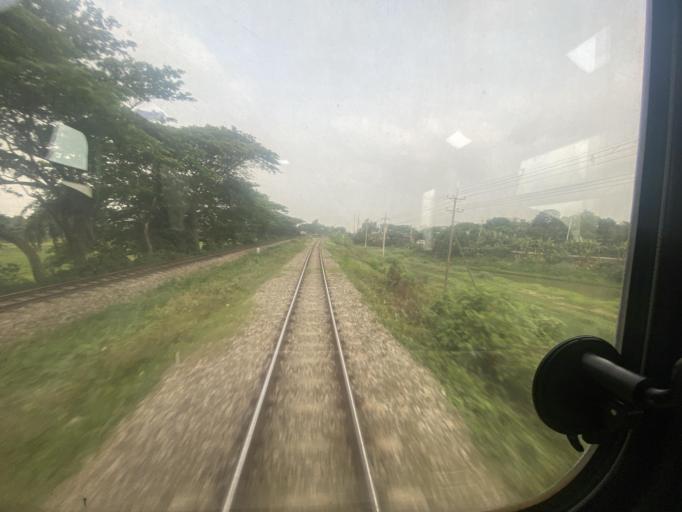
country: BD
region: Dhaka
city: Tungi
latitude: 23.9336
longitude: 90.4963
